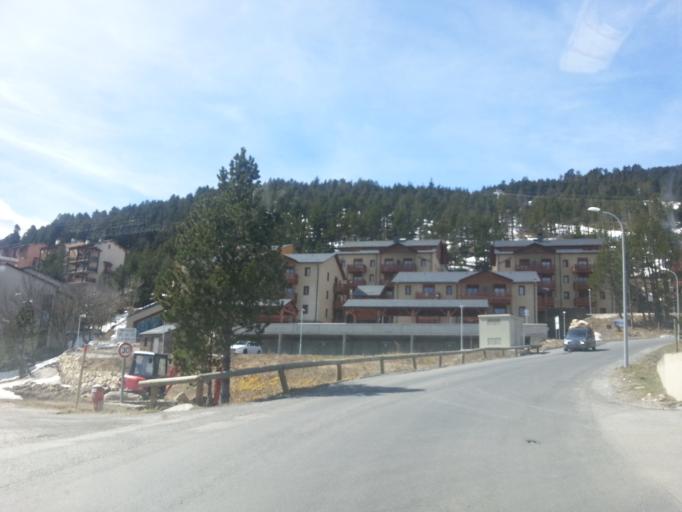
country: ES
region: Catalonia
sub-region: Provincia de Girona
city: Llivia
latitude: 42.5688
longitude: 2.0715
